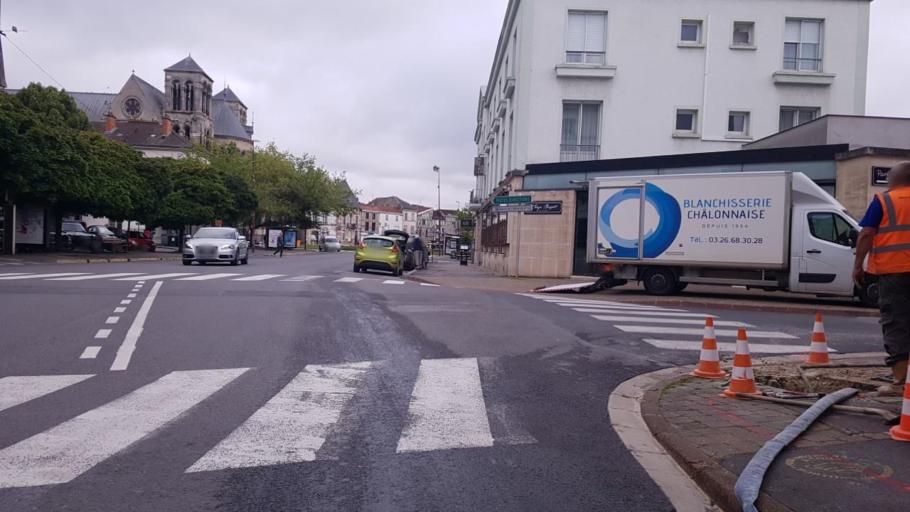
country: FR
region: Champagne-Ardenne
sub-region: Departement de la Marne
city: Chalons-en-Champagne
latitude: 48.9565
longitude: 4.3653
